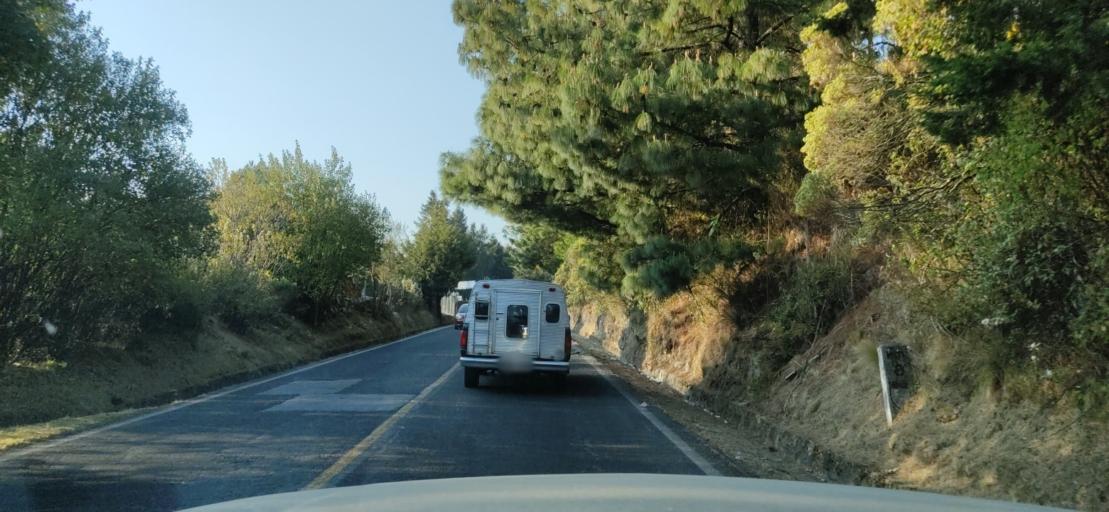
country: MX
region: Mexico
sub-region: Ocoyoacac
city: San Jeronimo Acazulco
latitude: 19.2454
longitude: -99.3713
